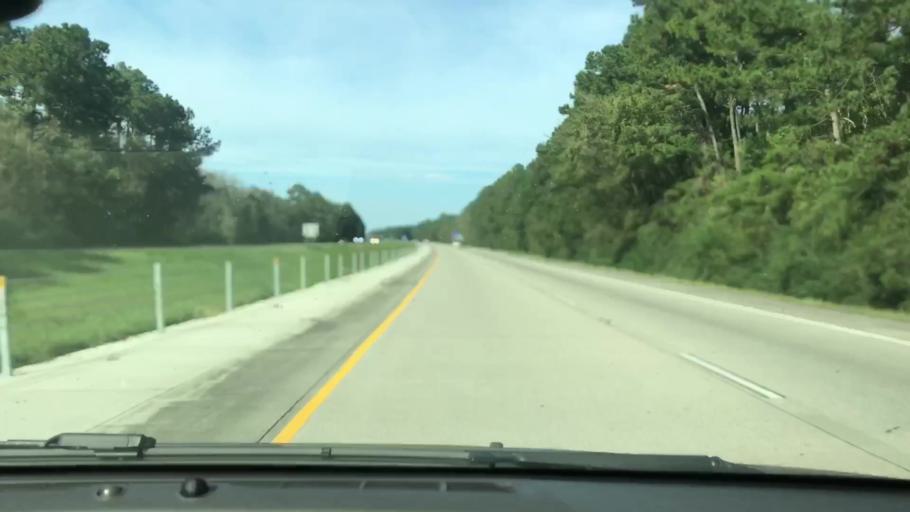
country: US
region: Louisiana
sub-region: Saint Tammany Parish
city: Pearl River
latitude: 30.3364
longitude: -89.7377
